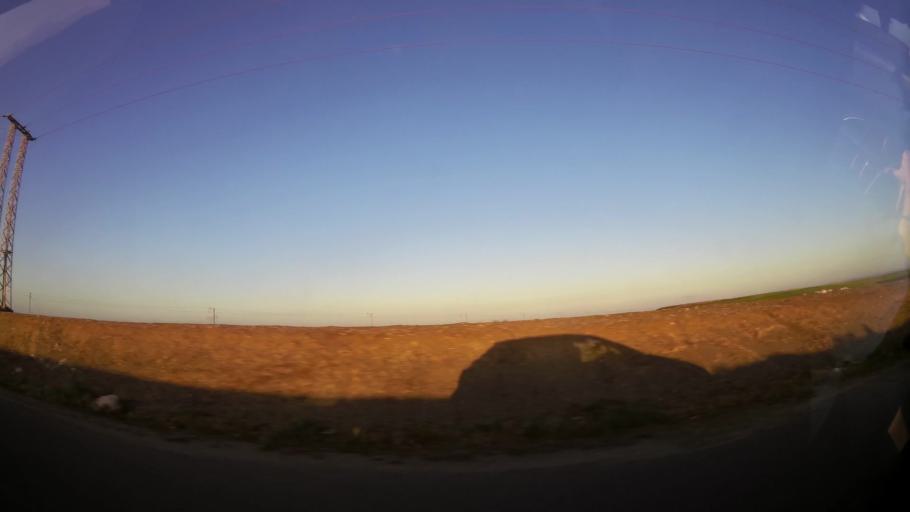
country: MA
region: Marrakech-Tensift-Al Haouz
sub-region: Kelaa-Des-Sraghna
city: Sidi Abdallah
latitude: 32.2379
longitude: -7.9282
